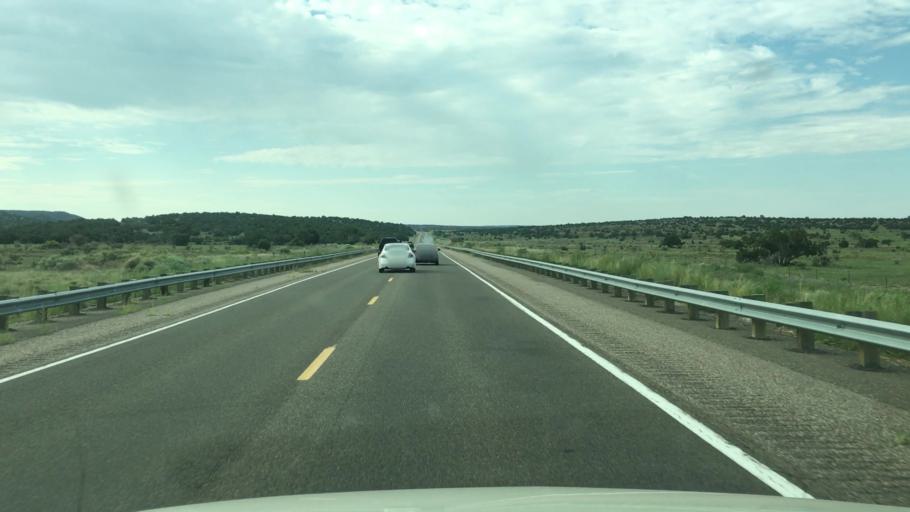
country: US
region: New Mexico
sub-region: Santa Fe County
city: Eldorado at Santa Fe
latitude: 35.3079
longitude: -105.8290
